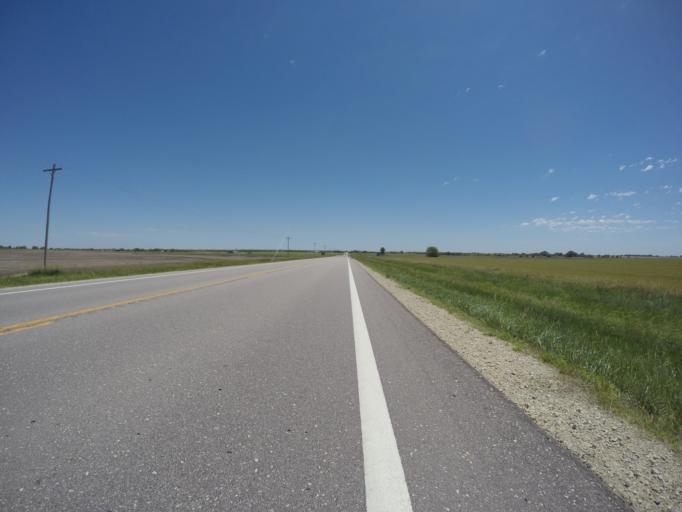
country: US
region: Kansas
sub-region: Republic County
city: Belleville
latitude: 39.8127
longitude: -97.6779
